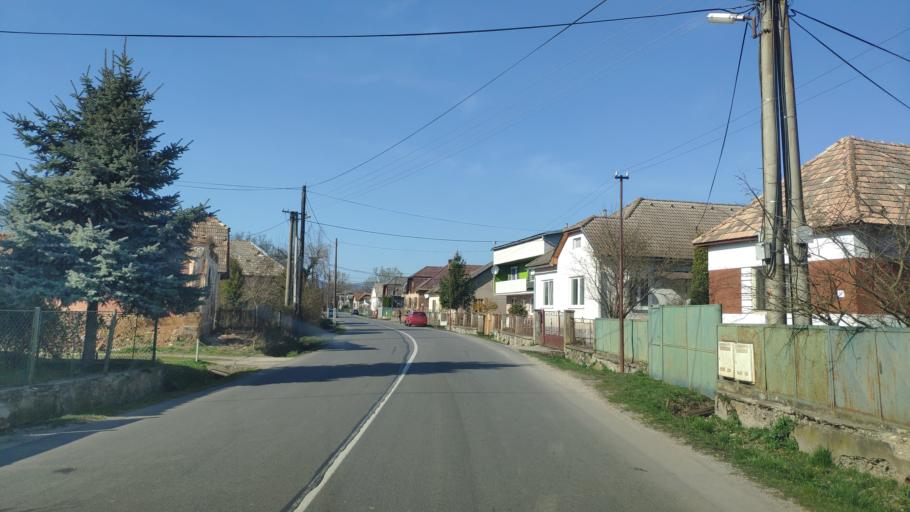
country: SK
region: Banskobystricky
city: Revuca
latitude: 48.5405
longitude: 20.2978
